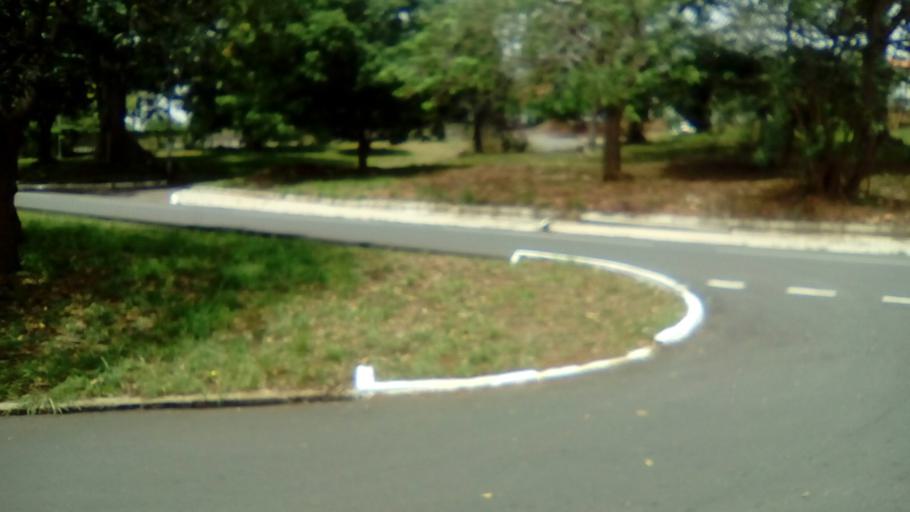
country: GH
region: Greater Accra
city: Medina Estates
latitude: 5.6499
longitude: -0.1906
